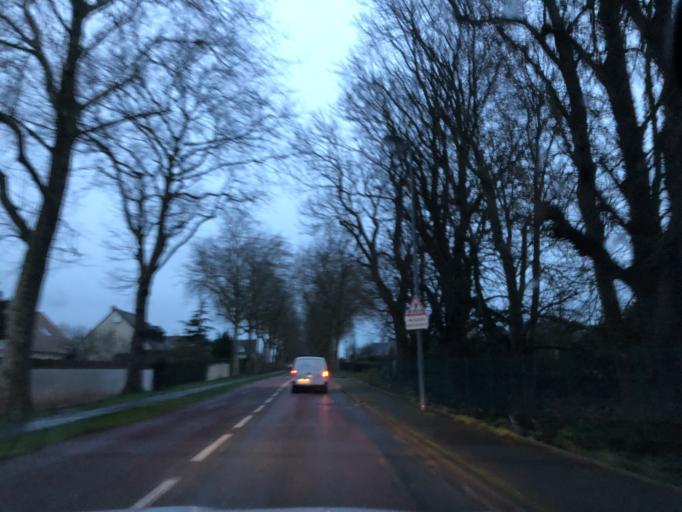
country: FR
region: Lower Normandy
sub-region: Departement du Calvados
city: Mathieu
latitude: 49.2579
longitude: -0.3740
